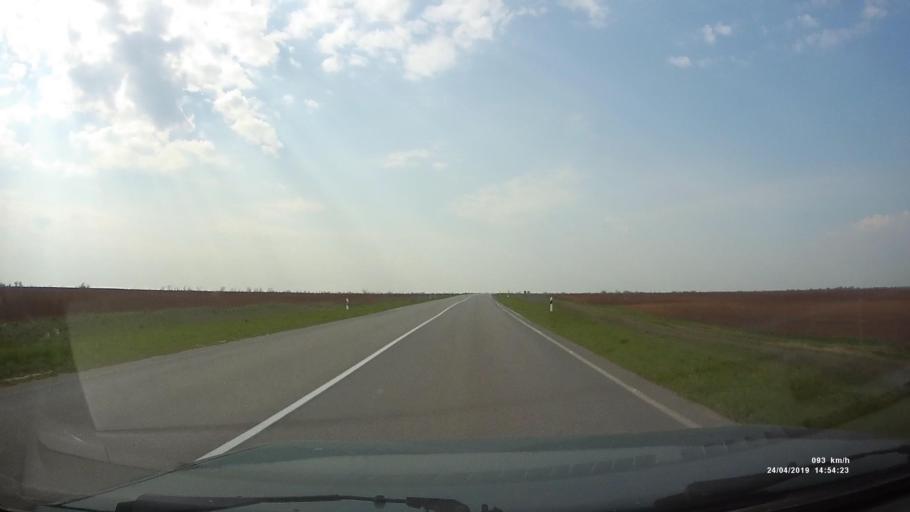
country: RU
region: Rostov
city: Remontnoye
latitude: 46.5341
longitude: 43.6394
